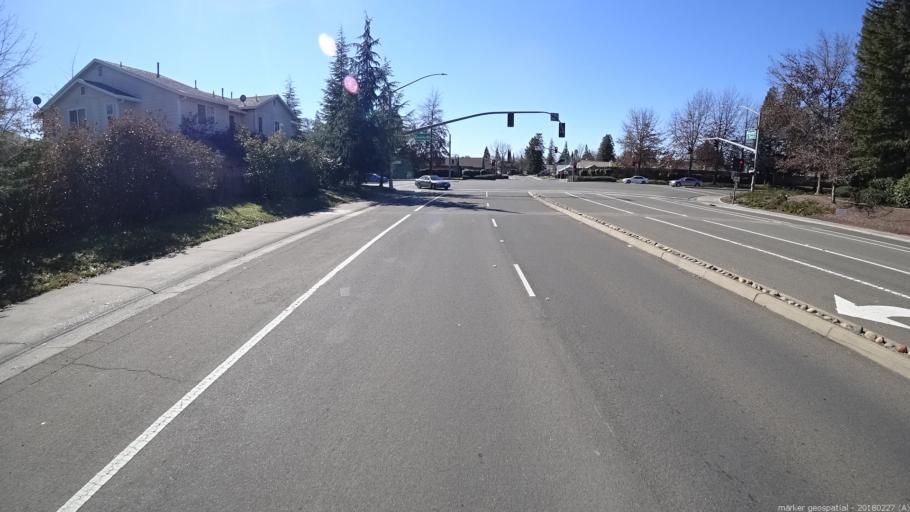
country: US
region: California
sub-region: Sacramento County
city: North Highlands
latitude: 38.7170
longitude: -121.3740
